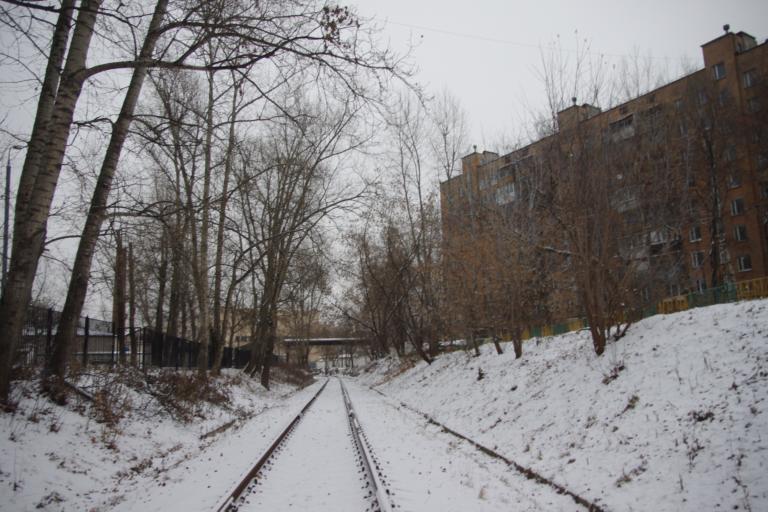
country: RU
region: Moscow
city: Nagornyy
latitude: 55.6599
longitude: 37.6254
